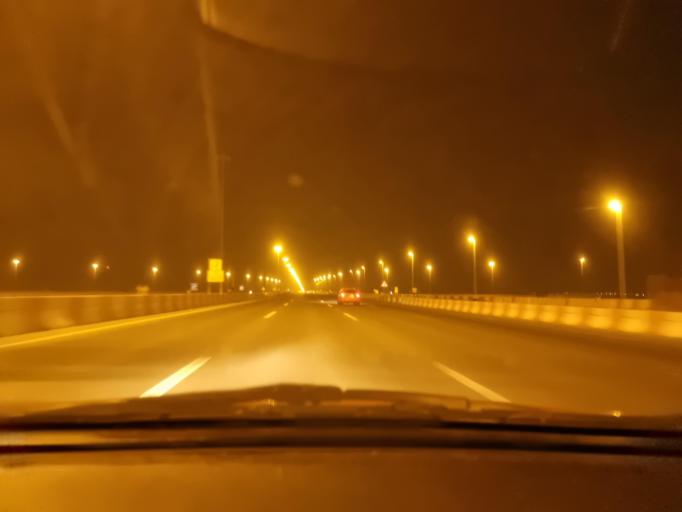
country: AE
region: Abu Dhabi
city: Abu Dhabi
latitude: 24.6762
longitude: 54.8159
